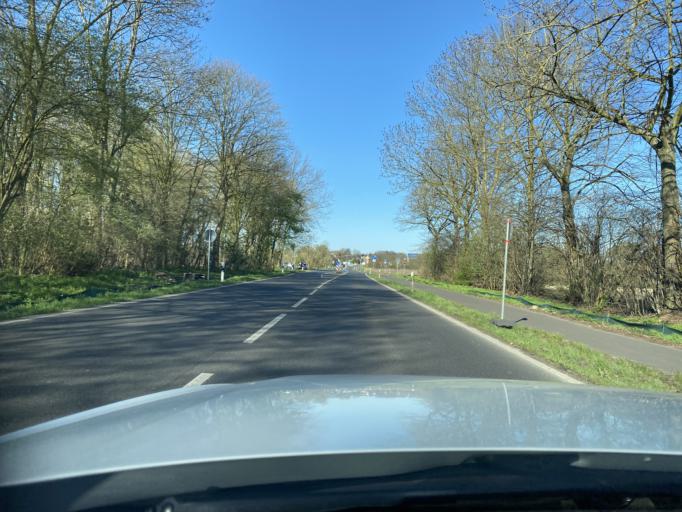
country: DE
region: North Rhine-Westphalia
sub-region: Regierungsbezirk Dusseldorf
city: Grevenbroich
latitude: 51.1018
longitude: 6.5968
